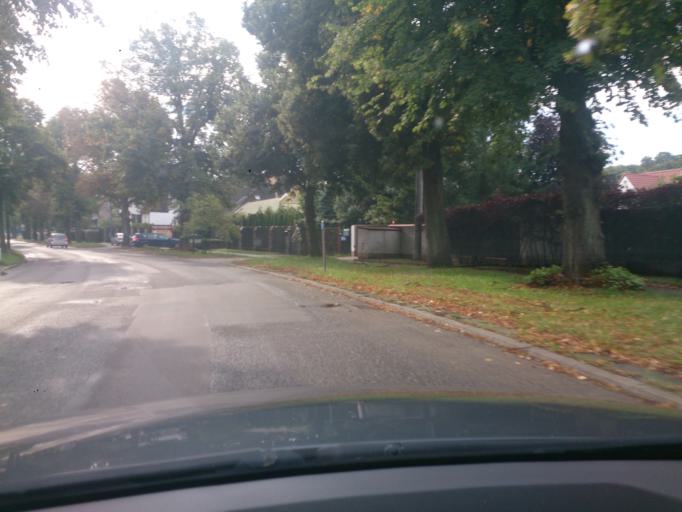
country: PL
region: Pomeranian Voivodeship
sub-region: Sopot
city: Sopot
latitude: 54.3919
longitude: 18.5693
